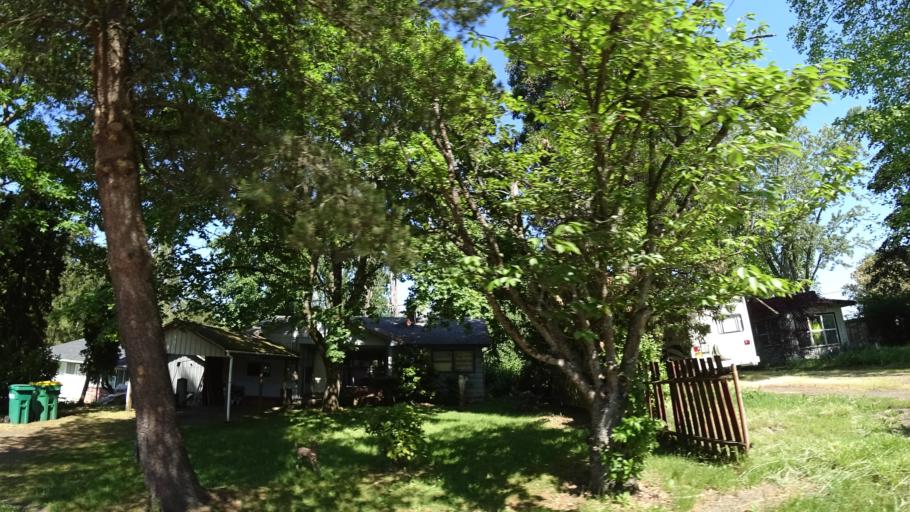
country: US
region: Oregon
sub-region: Washington County
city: Beaverton
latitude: 45.4916
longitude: -122.8247
